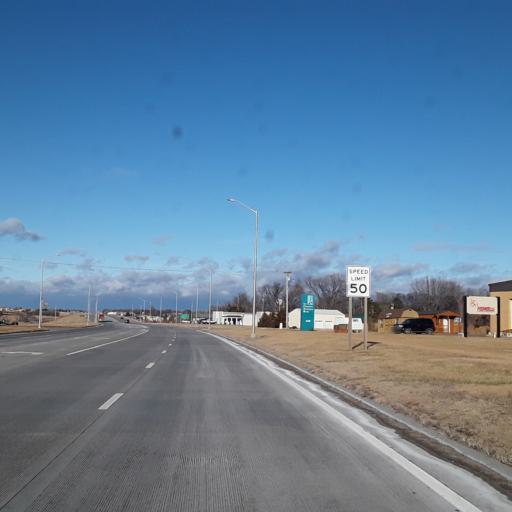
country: US
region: Kansas
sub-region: Republic County
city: Belleville
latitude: 39.8206
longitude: -97.6403
